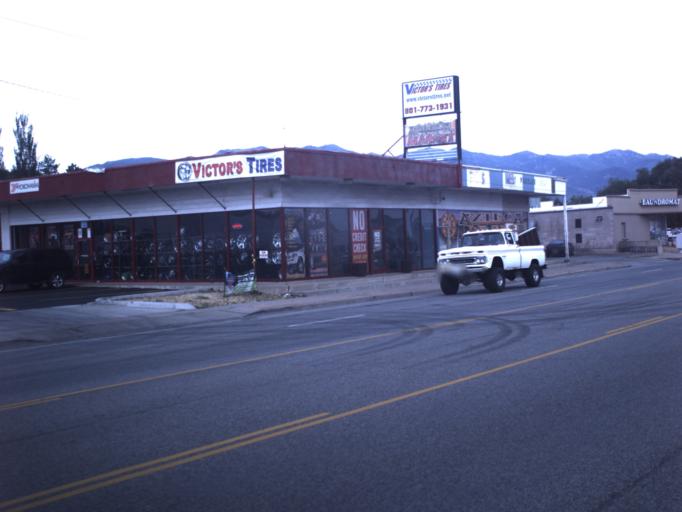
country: US
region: Utah
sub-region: Davis County
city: Clearfield
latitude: 41.1066
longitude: -112.0189
